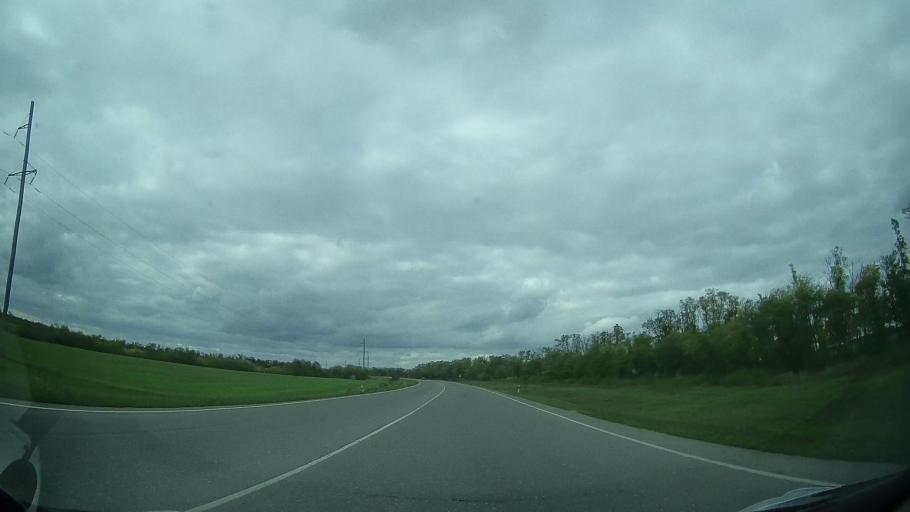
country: RU
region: Rostov
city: Mechetinskaya
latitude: 46.7837
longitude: 40.4114
